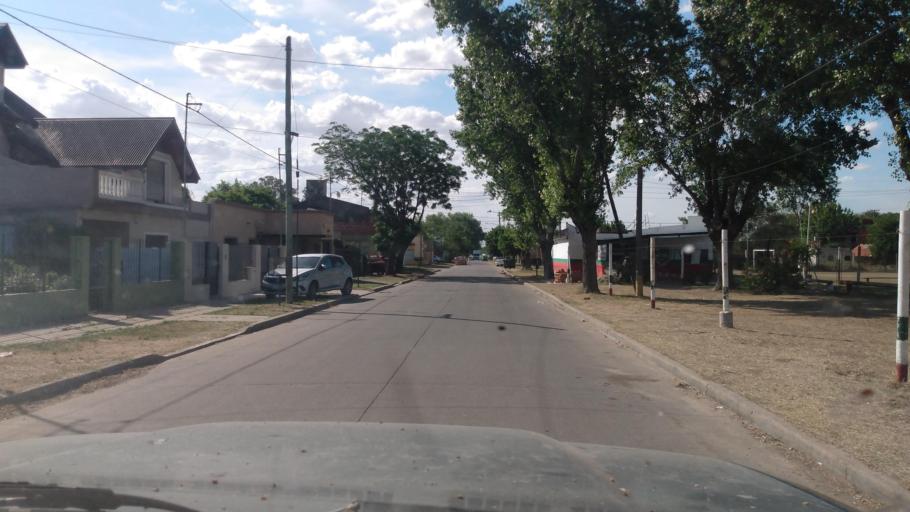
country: AR
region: Buenos Aires
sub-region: Partido de Lujan
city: Lujan
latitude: -34.5546
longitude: -59.1091
